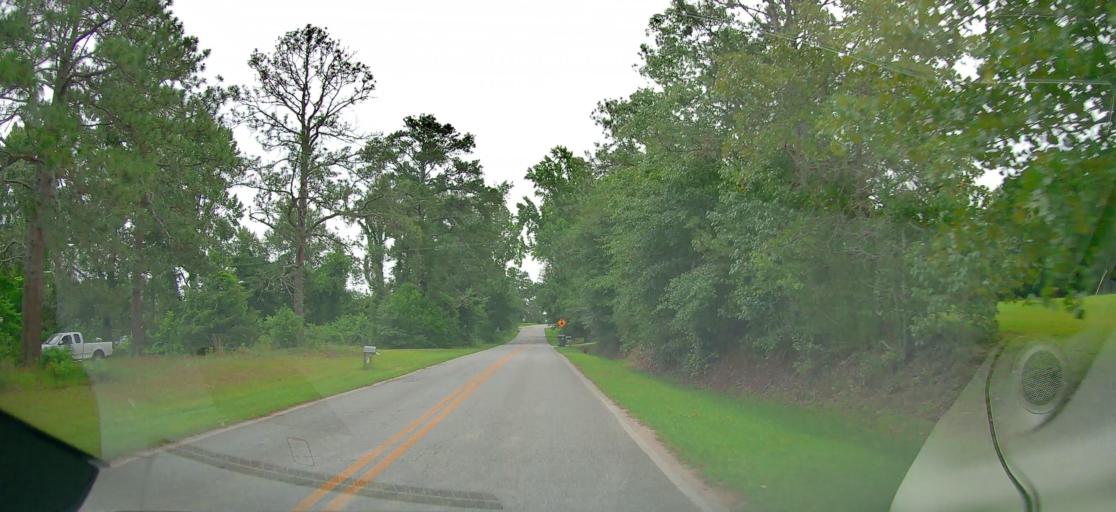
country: US
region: Georgia
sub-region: Bibb County
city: West Point
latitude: 32.7703
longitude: -83.7799
